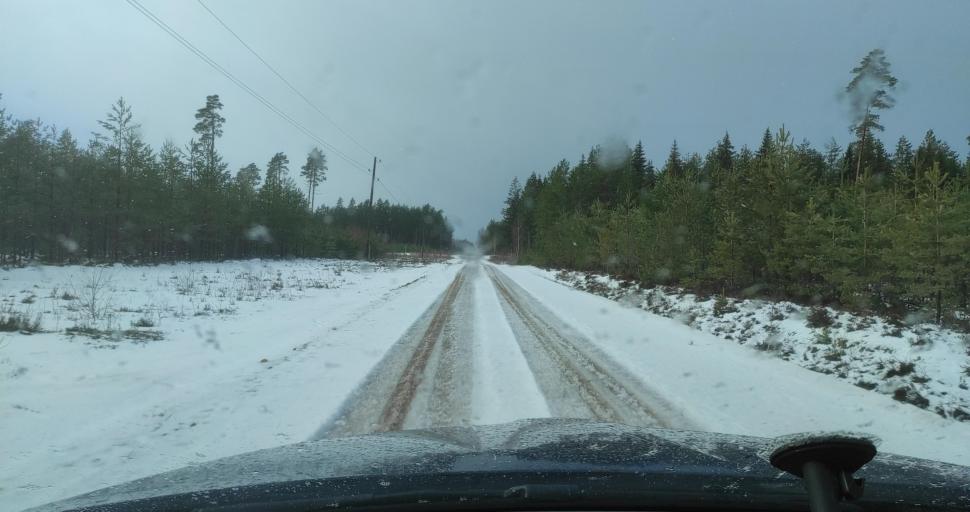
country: LV
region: Dundaga
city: Dundaga
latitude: 57.3831
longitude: 22.1504
